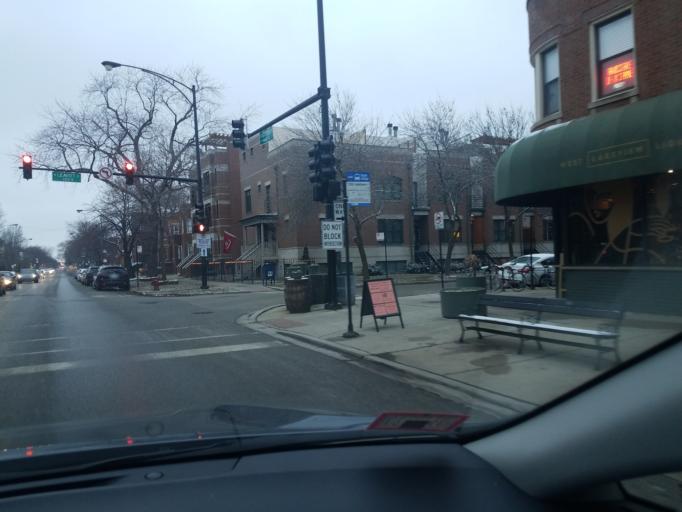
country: US
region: Illinois
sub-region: Cook County
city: Lincolnwood
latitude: 41.9469
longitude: -87.6832
